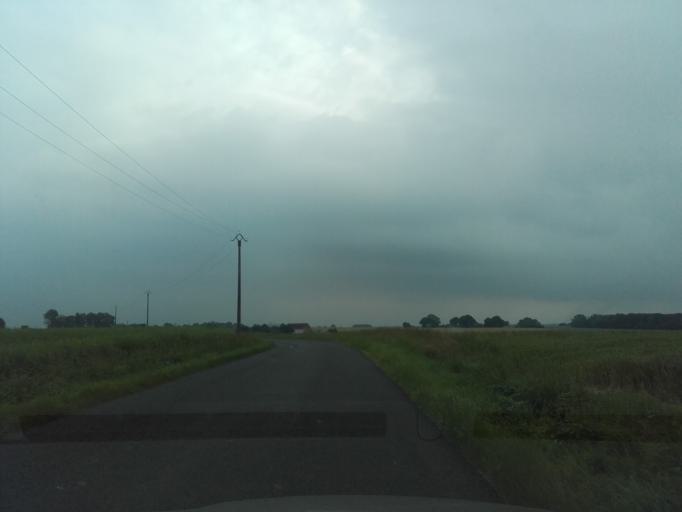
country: FR
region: Pays de la Loire
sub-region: Departement de la Sarthe
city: Ruille-sur-Loir
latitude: 47.6754
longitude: 0.6698
